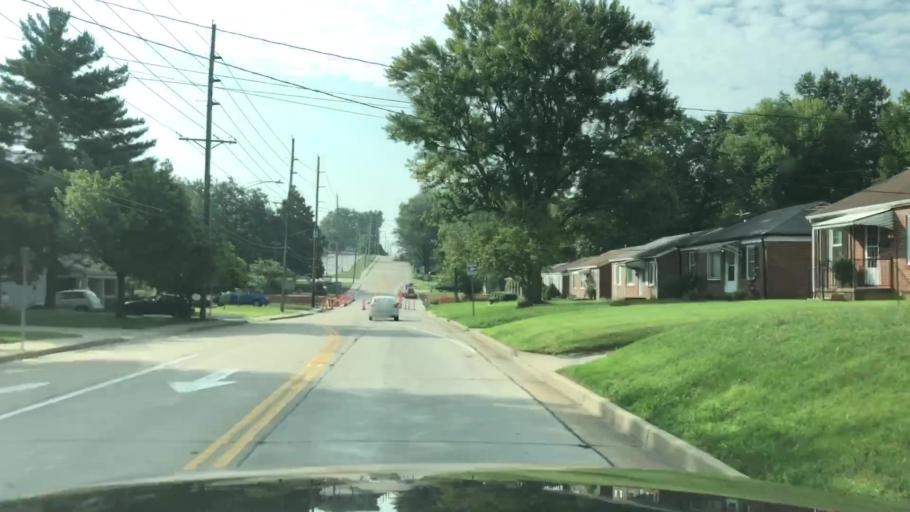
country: US
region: Missouri
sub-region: Saint Charles County
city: Saint Charles
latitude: 38.7941
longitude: -90.4988
